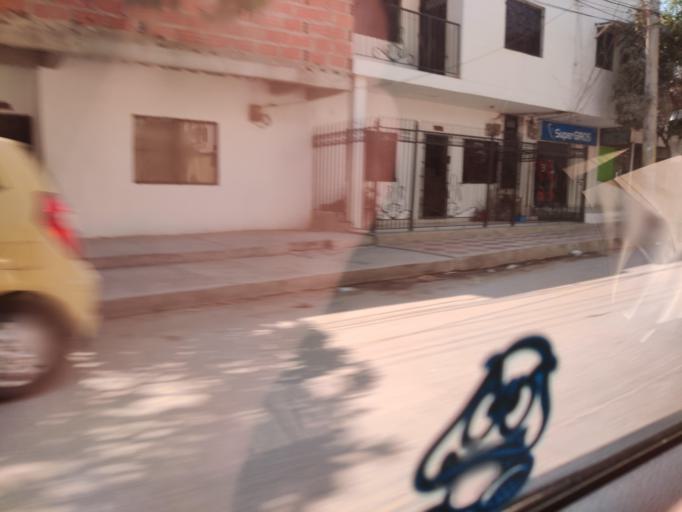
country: CO
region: Atlantico
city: Soledad
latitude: 10.9129
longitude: -74.8047
